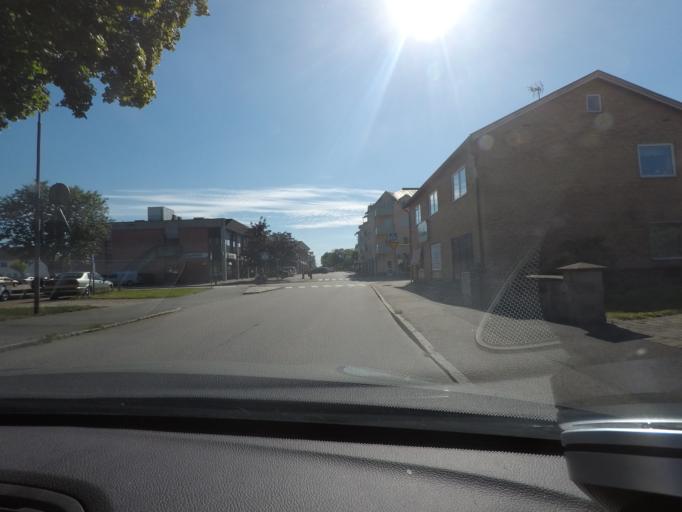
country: SE
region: Kronoberg
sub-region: Markaryds Kommun
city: Markaryd
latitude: 56.4622
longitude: 13.5978
